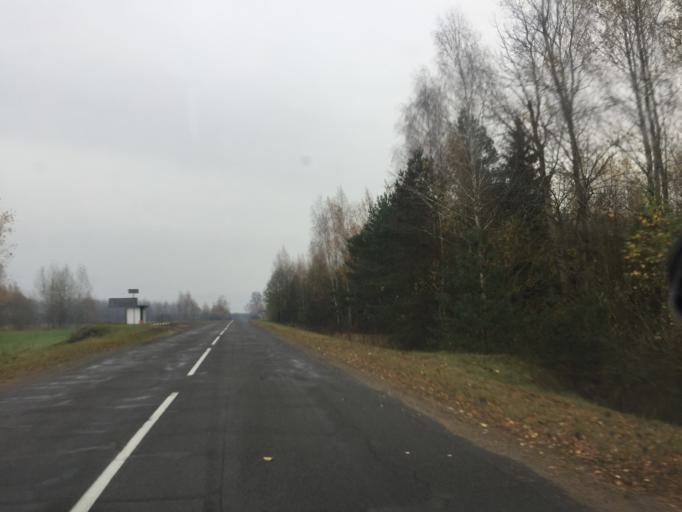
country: BY
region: Mogilev
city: Drybin
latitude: 54.0136
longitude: 31.0186
